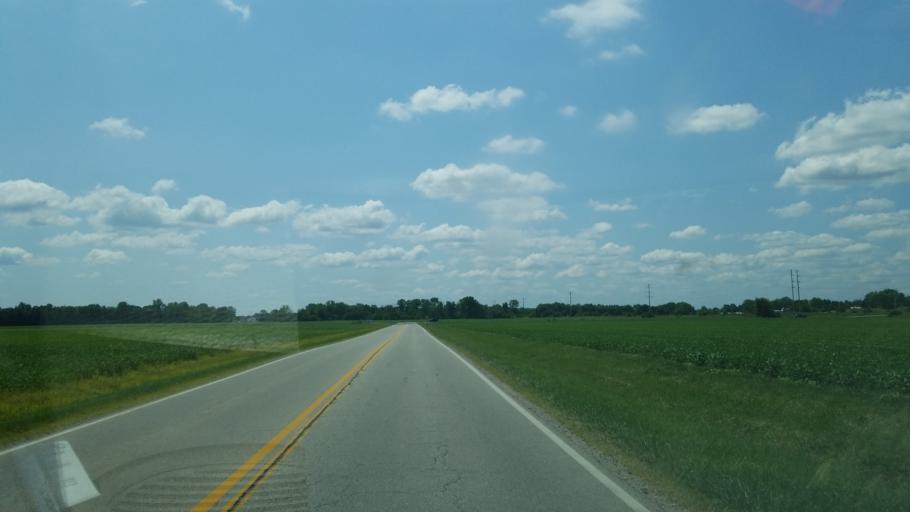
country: US
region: Ohio
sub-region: Delaware County
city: Lewis Center
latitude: 40.2157
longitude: -83.0076
